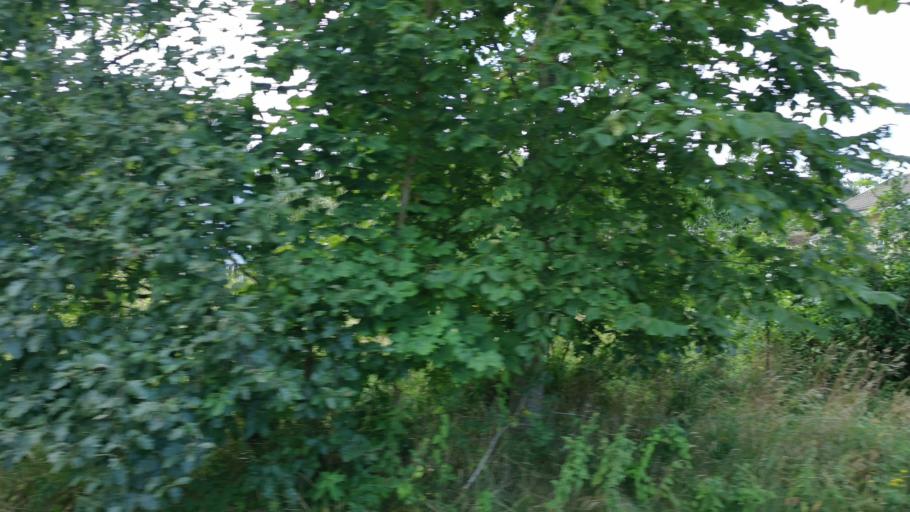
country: SE
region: Vaestra Goetaland
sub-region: Sotenas Kommun
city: Hunnebostrand
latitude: 58.5332
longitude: 11.2877
